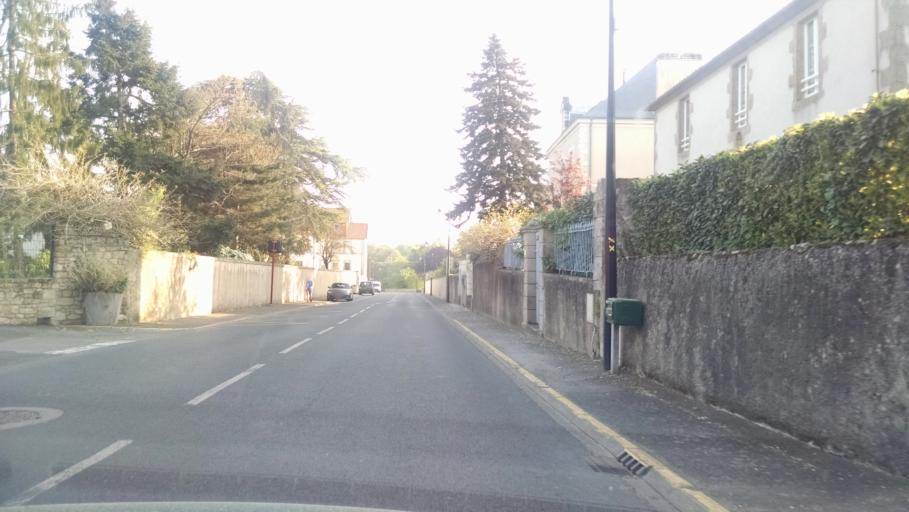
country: FR
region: Pays de la Loire
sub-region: Departement de la Loire-Atlantique
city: Boussay
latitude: 47.0414
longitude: -1.1881
